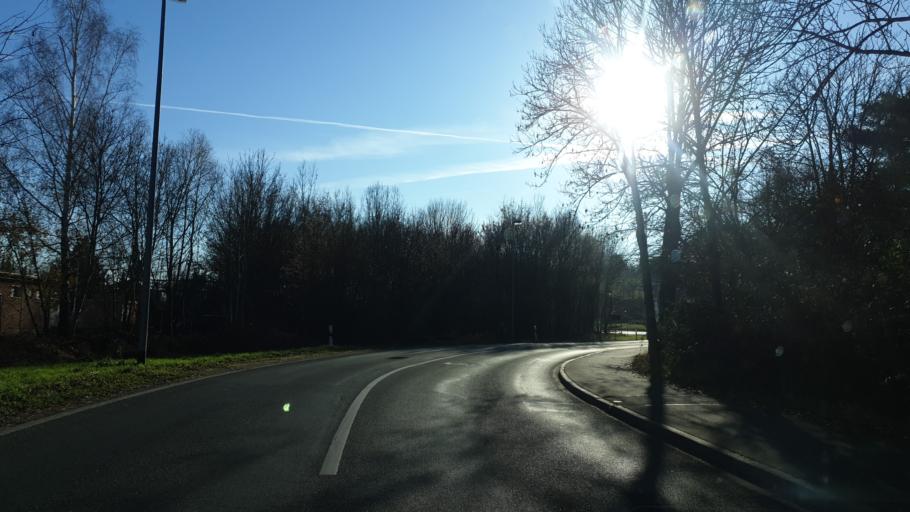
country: DE
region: Thuringia
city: Hartmannsdorf
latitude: 50.9645
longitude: 11.9839
